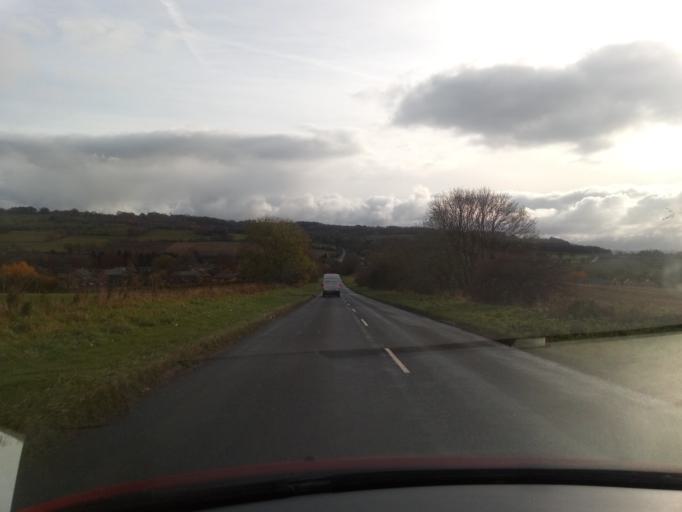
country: GB
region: England
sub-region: Northumberland
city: Wall
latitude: 55.0341
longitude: -2.1330
